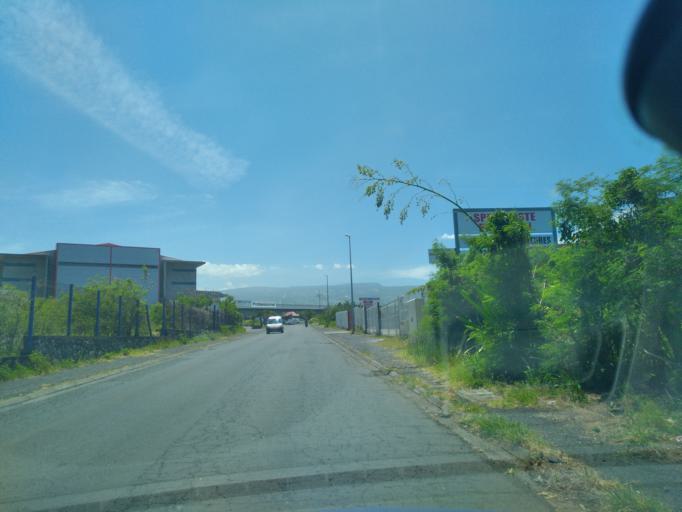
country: RE
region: Reunion
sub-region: Reunion
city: Saint-Pierre
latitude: -21.3207
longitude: 55.4497
